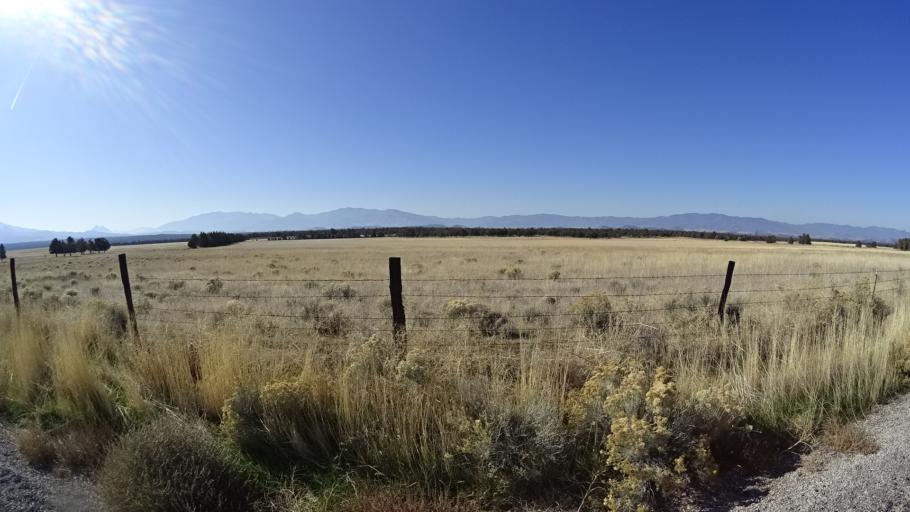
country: US
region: California
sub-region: Siskiyou County
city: Weed
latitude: 41.6179
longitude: -122.3202
